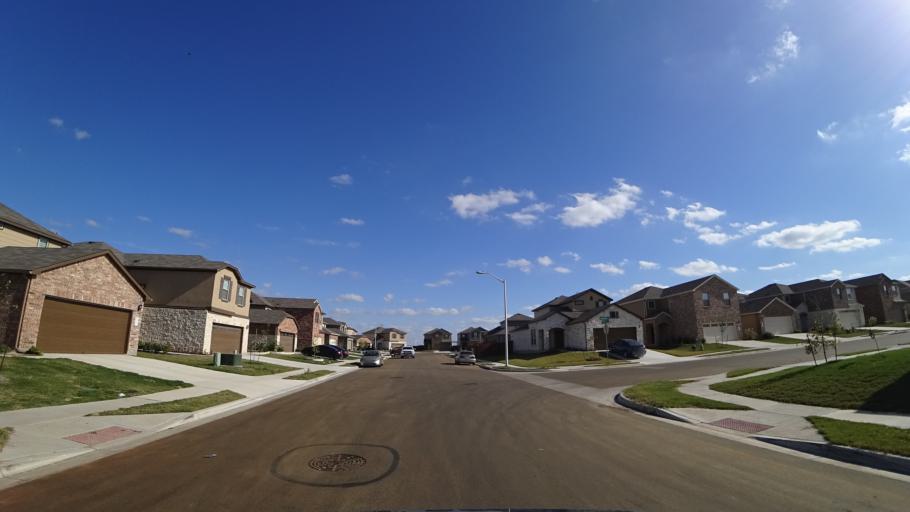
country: US
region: Texas
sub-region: Travis County
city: Wells Branch
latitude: 30.4680
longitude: -97.6808
